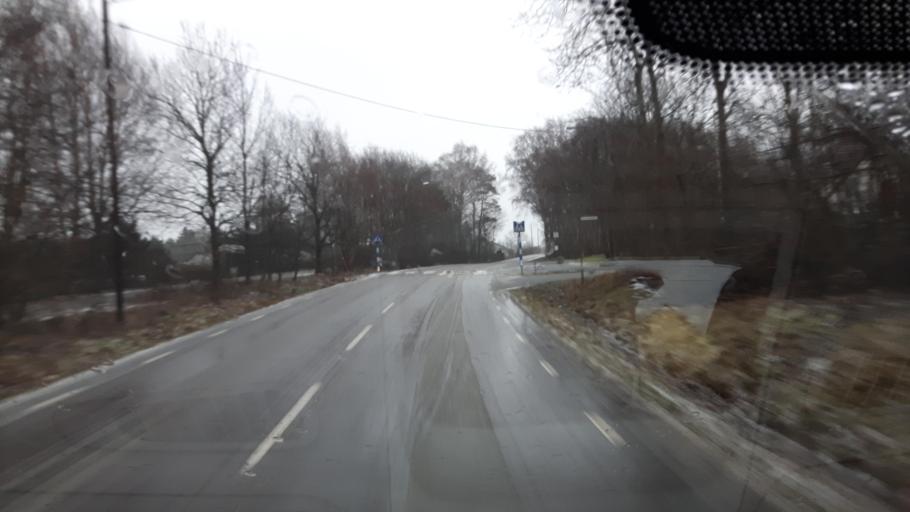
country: SE
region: Halland
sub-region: Kungsbacka Kommun
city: Onsala
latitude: 57.4119
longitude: 12.0104
